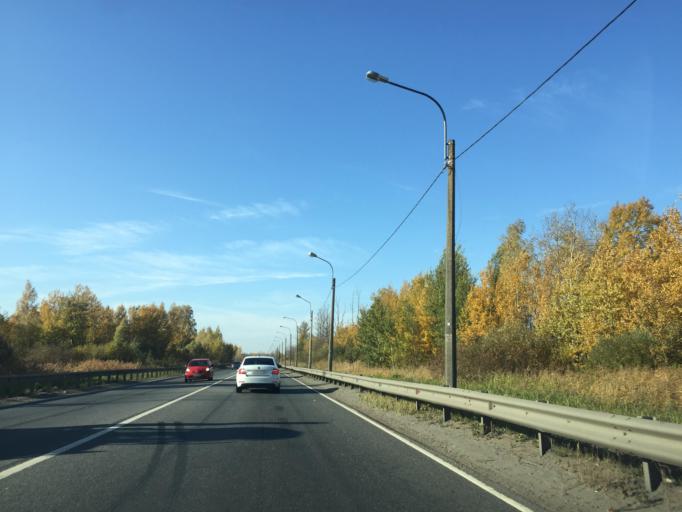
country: RU
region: St.-Petersburg
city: Petro-Slavyanka
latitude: 59.7480
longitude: 30.5200
